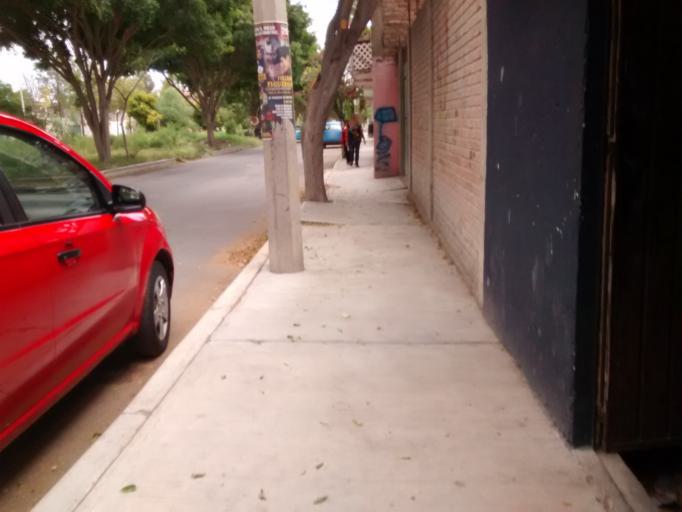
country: MX
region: Puebla
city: Tehuacan
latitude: 18.4723
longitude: -97.4065
